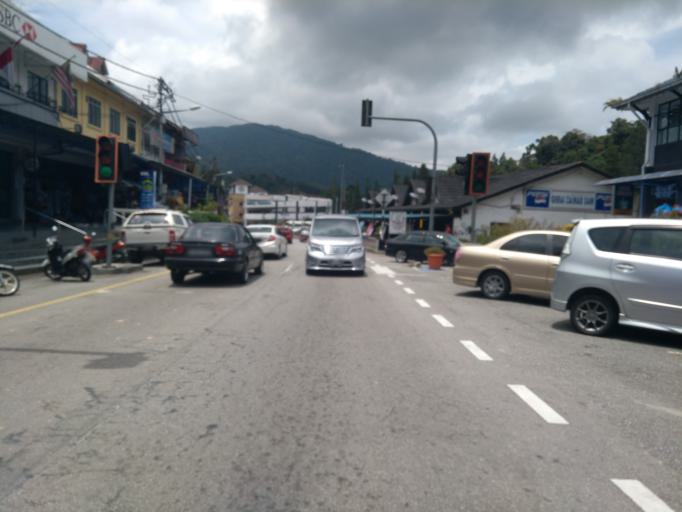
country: MY
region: Pahang
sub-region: Cameron Highlands
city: Tanah Rata
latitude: 4.4705
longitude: 101.3772
